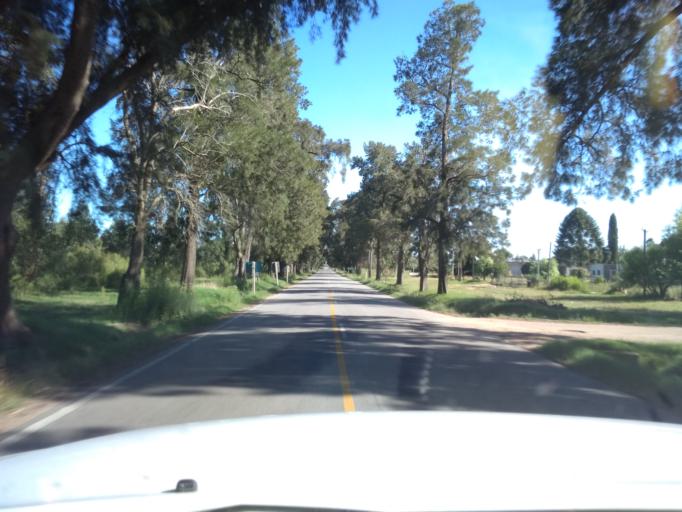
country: UY
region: Canelones
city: San Bautista
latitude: -34.3785
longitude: -55.9595
